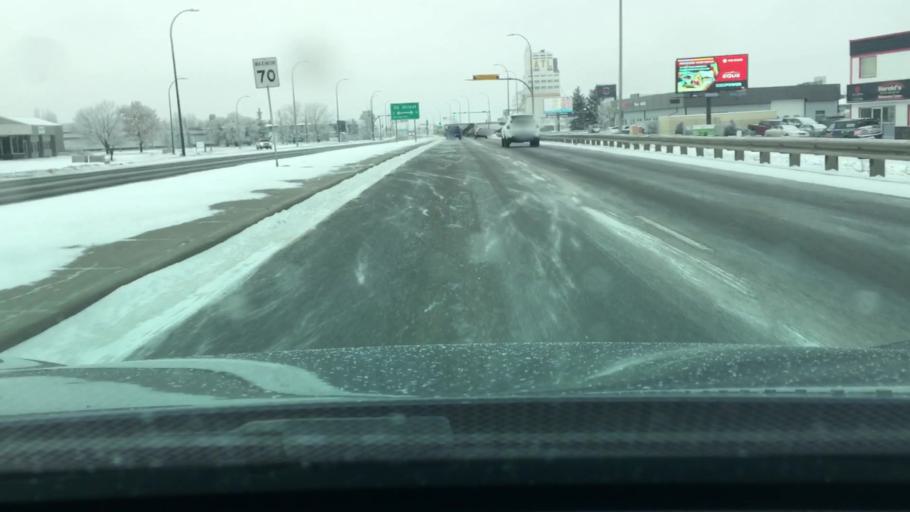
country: CA
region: Alberta
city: Lethbridge
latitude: 49.6983
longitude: -112.7931
